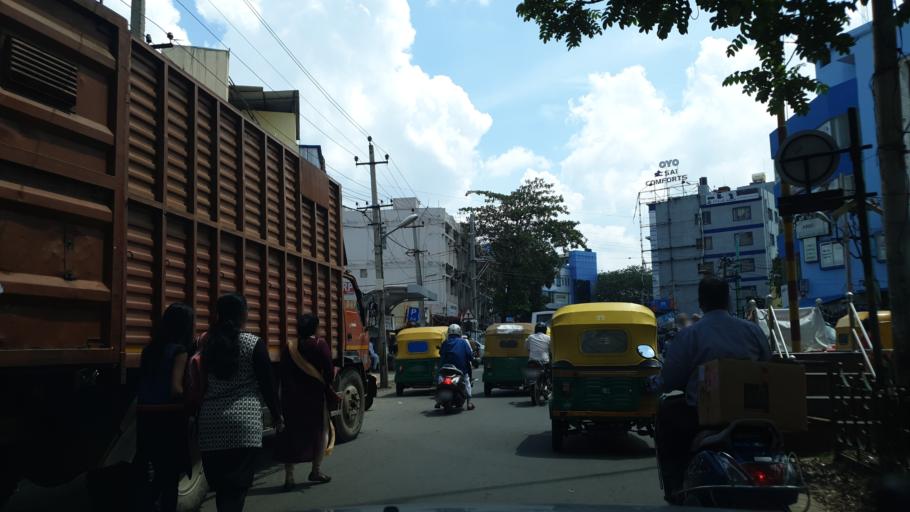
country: IN
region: Karnataka
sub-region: Bangalore Urban
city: Bangalore
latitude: 13.0290
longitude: 77.5614
